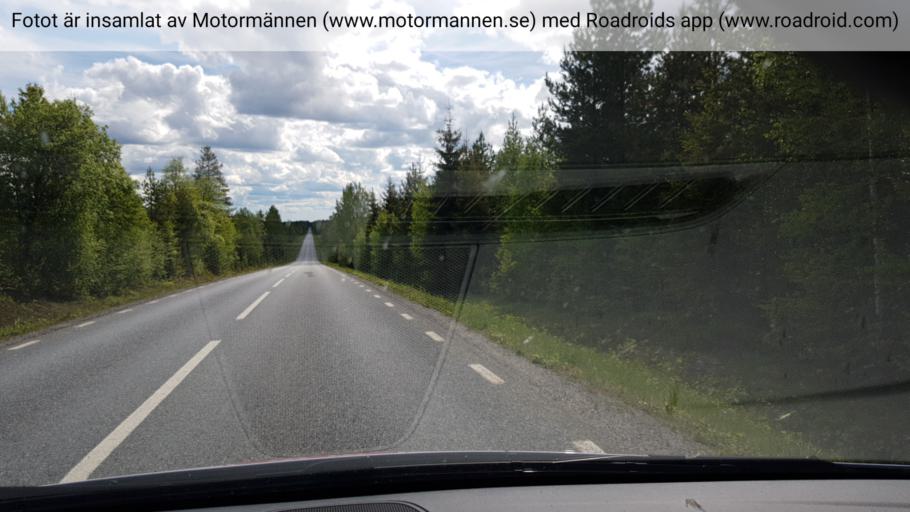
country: SE
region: Vaesterbotten
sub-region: Skelleftea Kommun
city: Burtraesk
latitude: 64.3731
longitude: 20.2501
